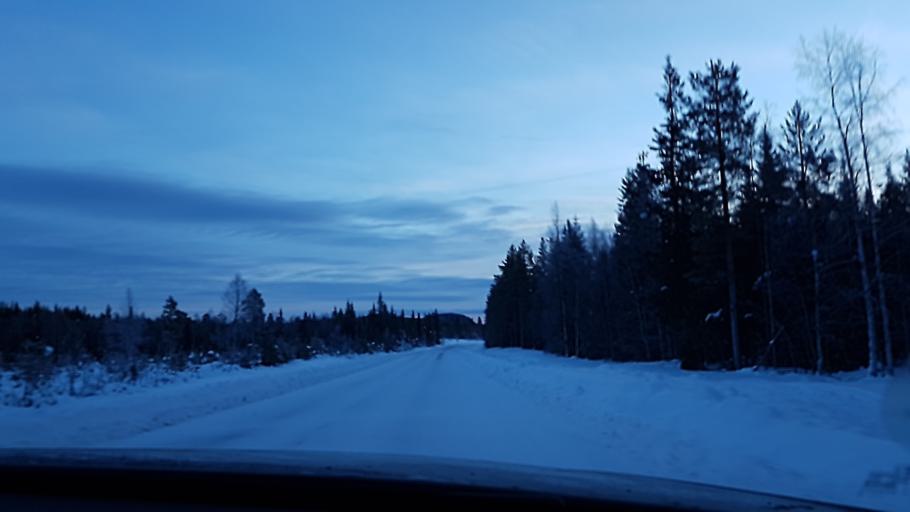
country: SE
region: Norrbotten
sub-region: Jokkmokks Kommun
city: Jokkmokk
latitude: 66.1245
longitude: 20.0223
